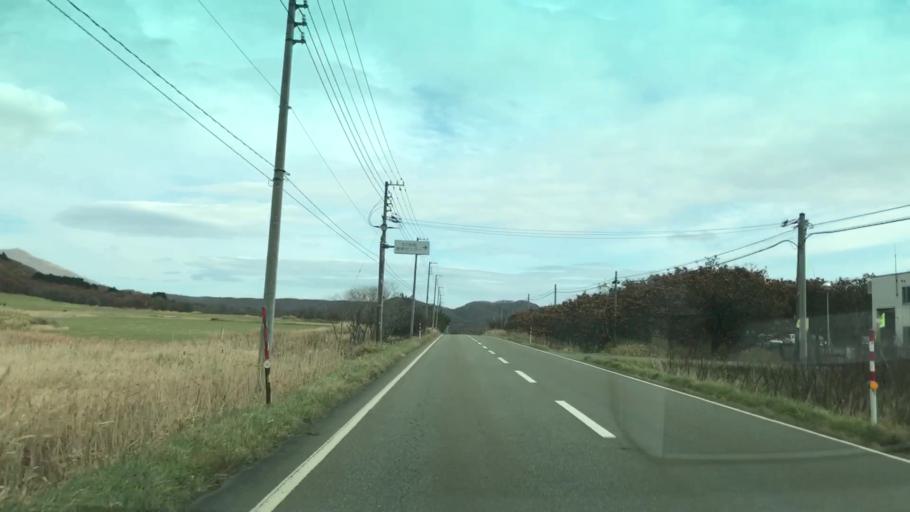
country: JP
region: Hokkaido
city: Shizunai-furukawacho
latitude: 42.0017
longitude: 143.1731
